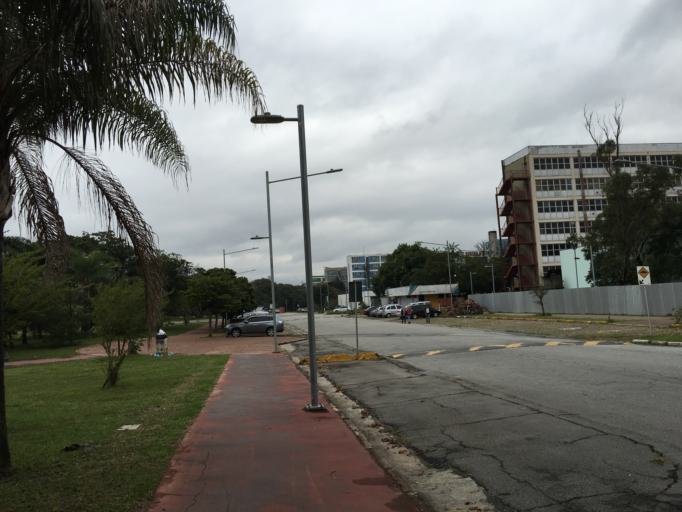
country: BR
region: Sao Paulo
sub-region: Osasco
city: Osasco
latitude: -23.5611
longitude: -46.7235
